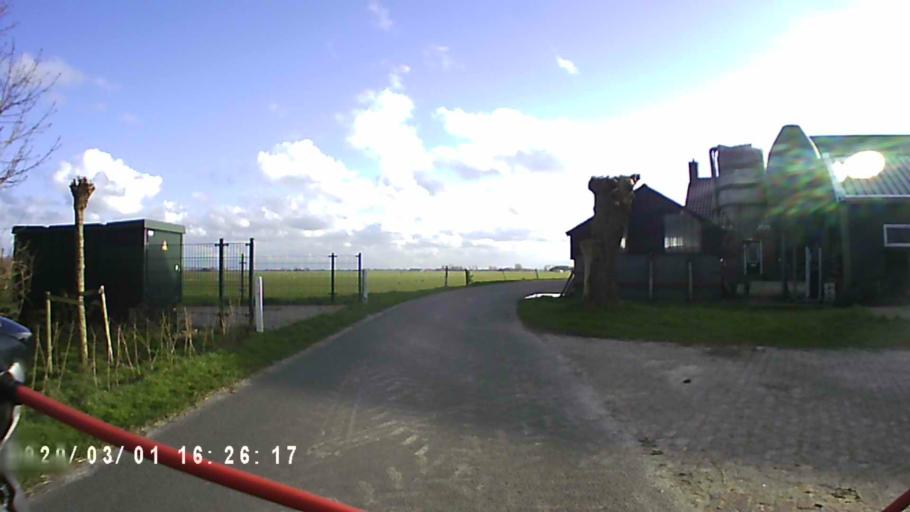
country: NL
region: Groningen
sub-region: Gemeente Zuidhorn
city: Oldehove
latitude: 53.3097
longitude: 6.4306
